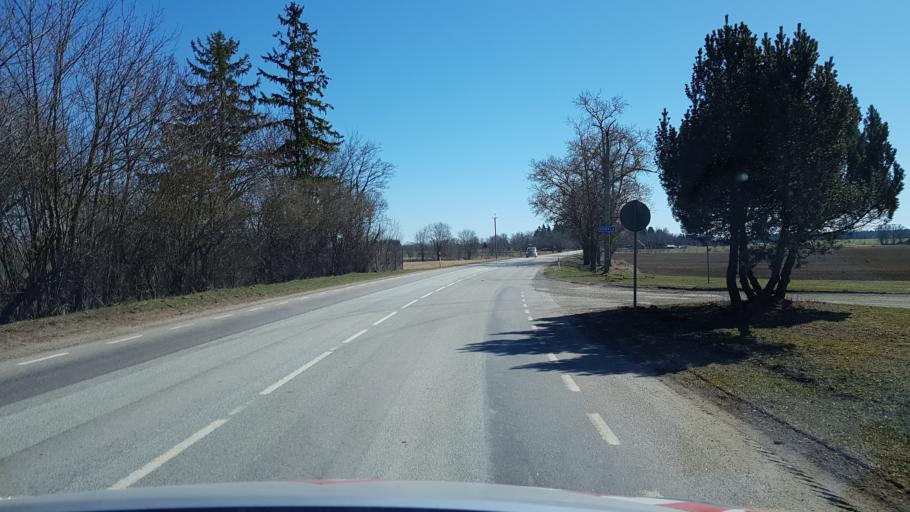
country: EE
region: Laeaene-Virumaa
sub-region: Viru-Nigula vald
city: Kunda
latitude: 59.4445
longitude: 26.6918
